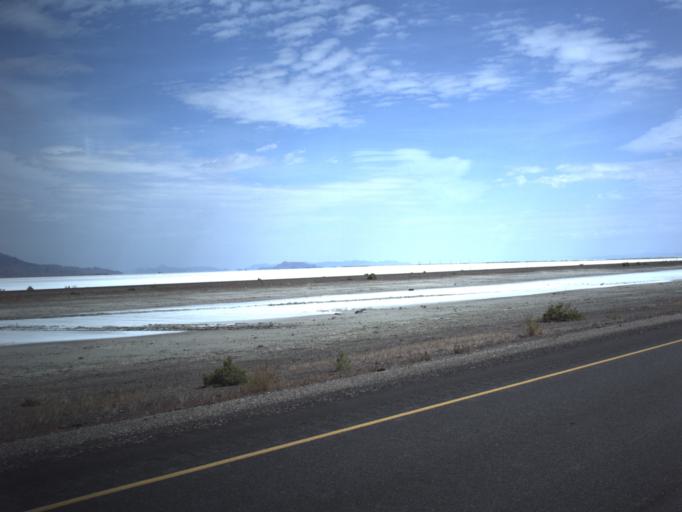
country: US
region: Utah
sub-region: Tooele County
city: Wendover
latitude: 40.7398
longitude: -113.9205
